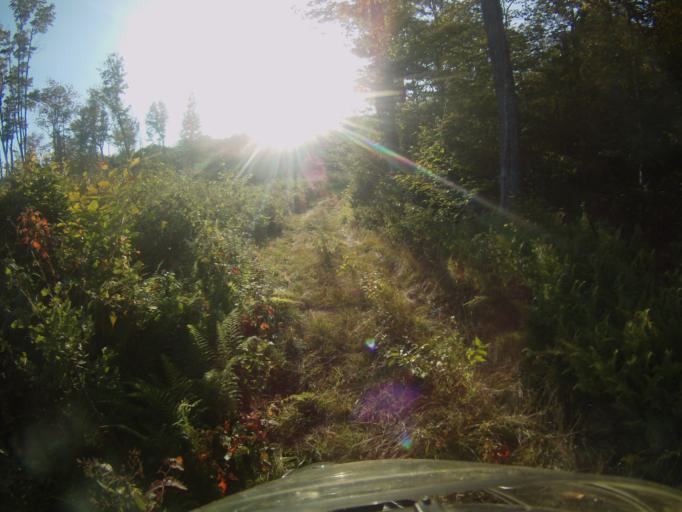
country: US
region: Vermont
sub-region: Addison County
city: Bristol
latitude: 44.0069
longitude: -73.0004
